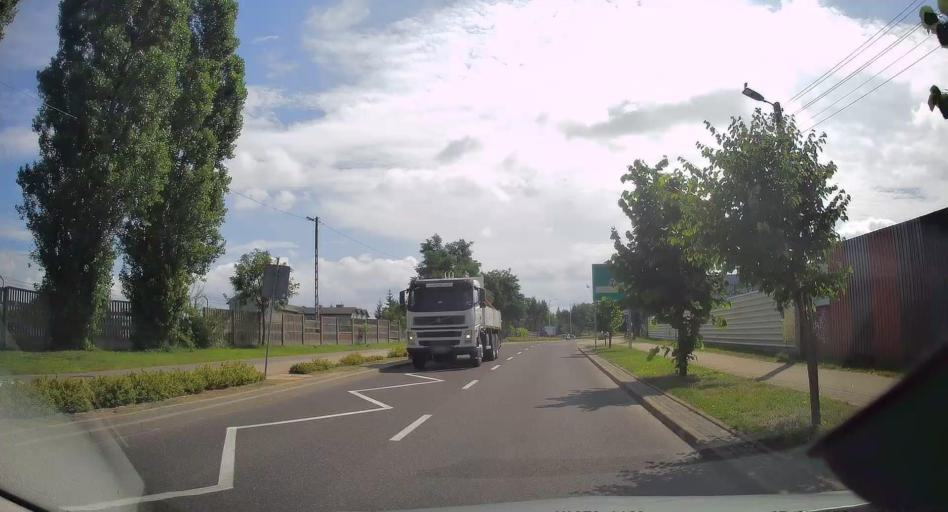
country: PL
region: Lodz Voivodeship
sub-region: Powiat rawski
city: Rawa Mazowiecka
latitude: 51.7525
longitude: 20.2391
